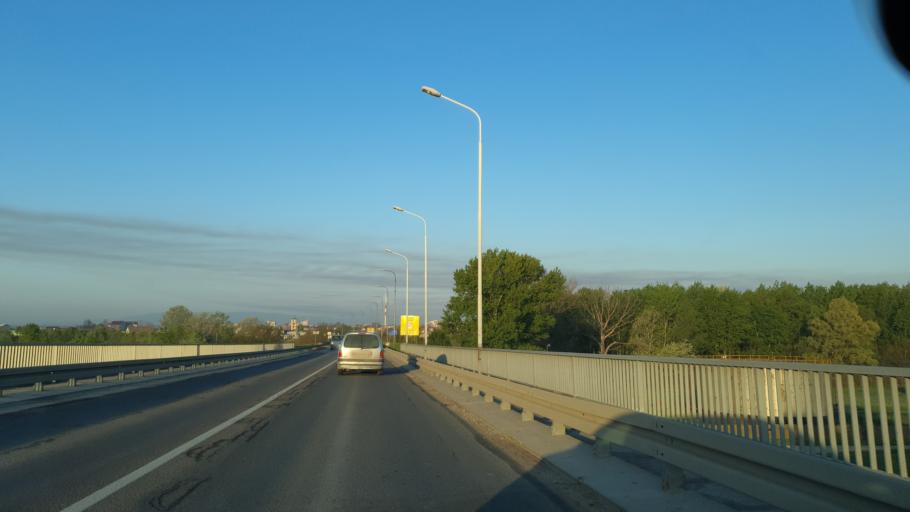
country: RS
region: Central Serbia
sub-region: Macvanski Okrug
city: Sabac
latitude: 44.7569
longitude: 19.7104
